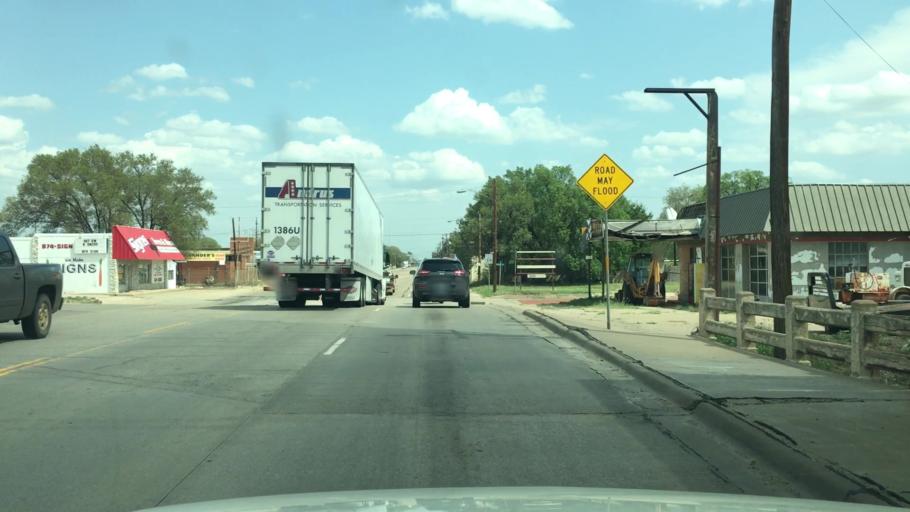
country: US
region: Texas
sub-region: Donley County
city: Clarendon
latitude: 34.9378
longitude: -100.8878
